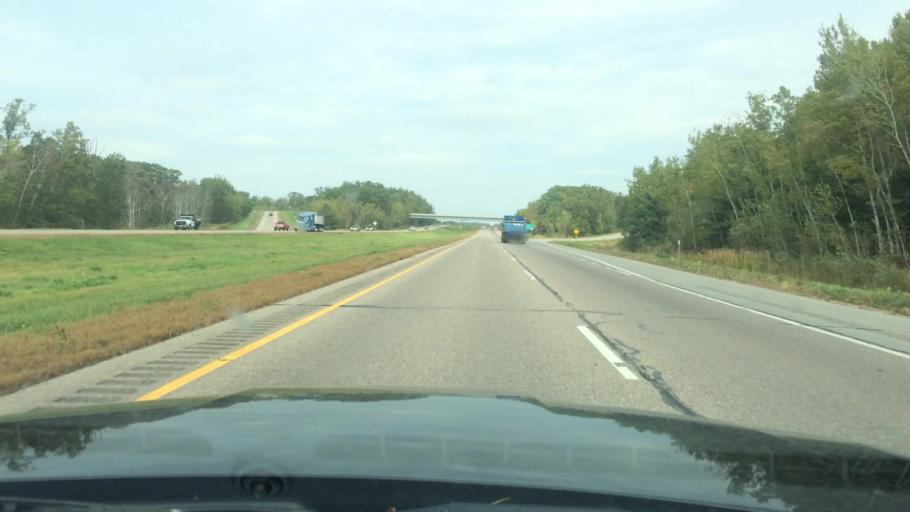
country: US
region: Wisconsin
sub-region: Marathon County
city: Mosinee
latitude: 44.6709
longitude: -89.6421
